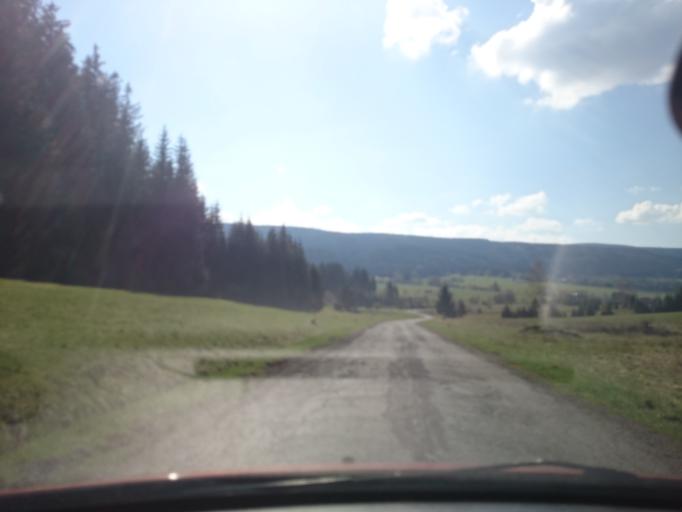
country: PL
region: Lower Silesian Voivodeship
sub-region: Powiat klodzki
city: Polanica-Zdroj
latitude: 50.2980
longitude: 16.4726
